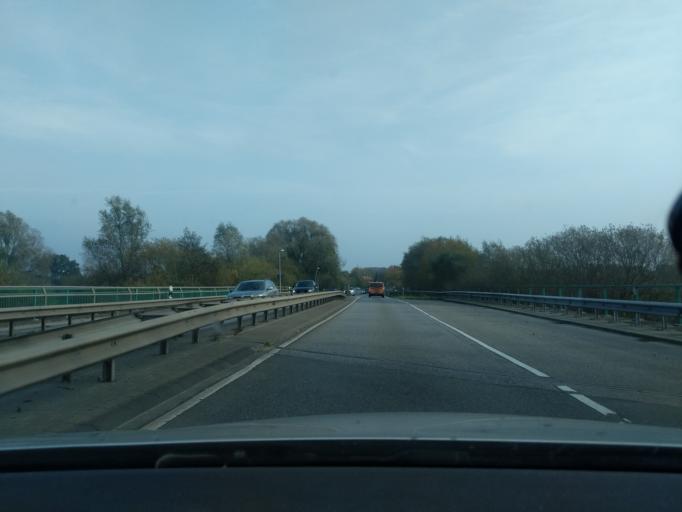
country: DE
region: Lower Saxony
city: Stade
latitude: 53.5902
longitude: 9.4484
